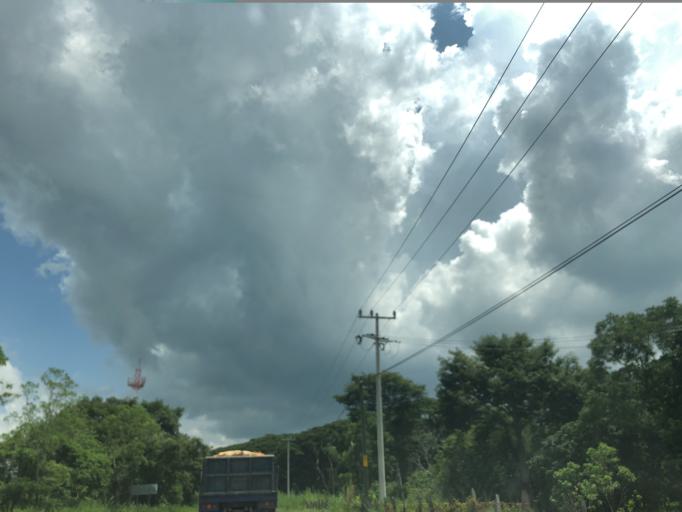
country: MX
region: Tabasco
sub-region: Comalcalco
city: Oriente 6ta. Seccion (Los Mulatos)
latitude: 18.1724
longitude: -93.2401
